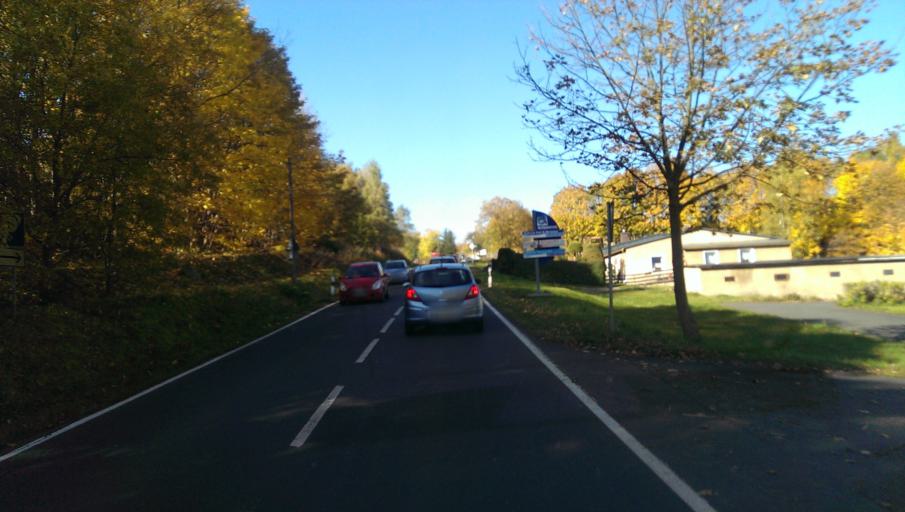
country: DE
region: Saxony
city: Altenberg
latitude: 50.7617
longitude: 13.7680
